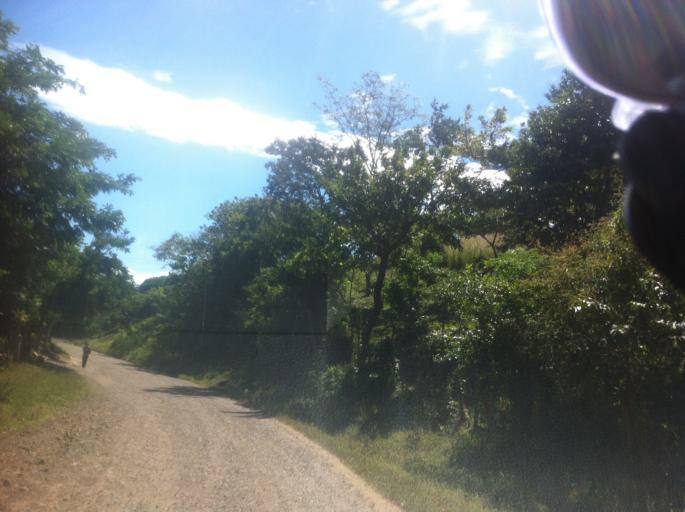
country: NI
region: Matagalpa
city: San Dionisio
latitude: 12.7838
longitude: -85.8503
